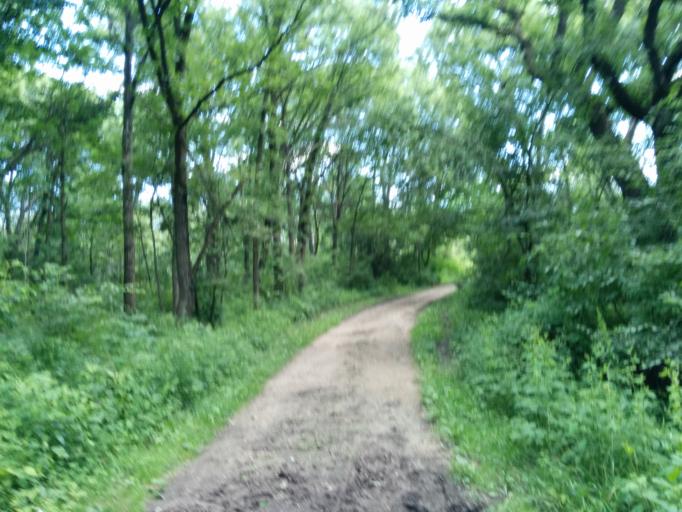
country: US
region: Illinois
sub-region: Will County
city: Goodings Grove
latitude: 41.6811
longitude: -87.8993
